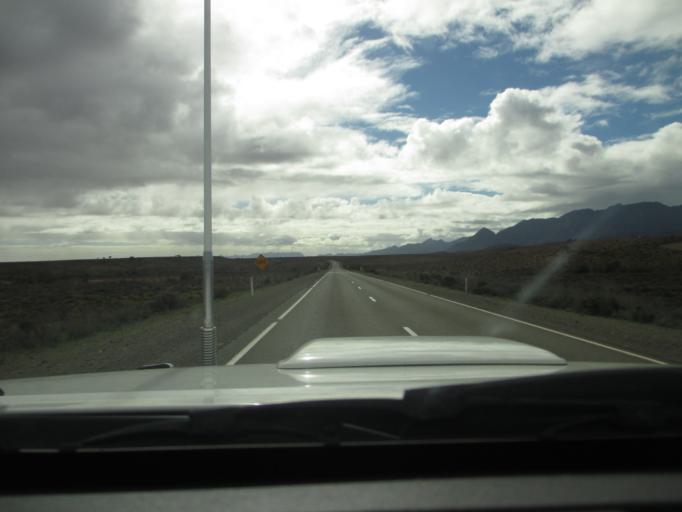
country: AU
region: South Australia
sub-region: Flinders Ranges
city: Quorn
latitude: -31.5715
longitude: 138.4238
